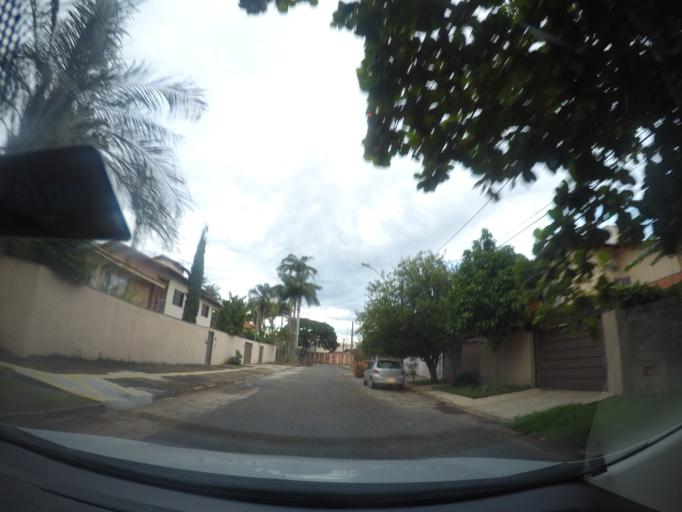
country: BR
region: Goias
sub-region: Goiania
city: Goiania
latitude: -16.6508
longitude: -49.2259
